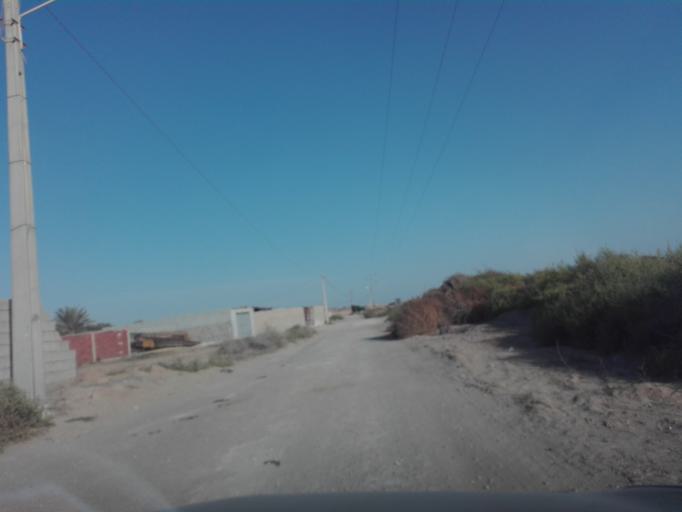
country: TN
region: Qabis
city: Gabes
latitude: 33.9587
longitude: 10.0623
